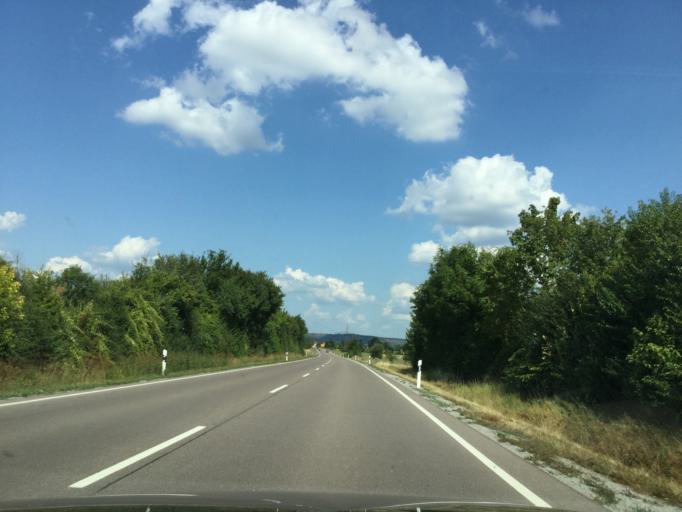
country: DE
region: Bavaria
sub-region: Regierungsbezirk Mittelfranken
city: Bad Windsheim
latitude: 49.4928
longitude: 10.4257
